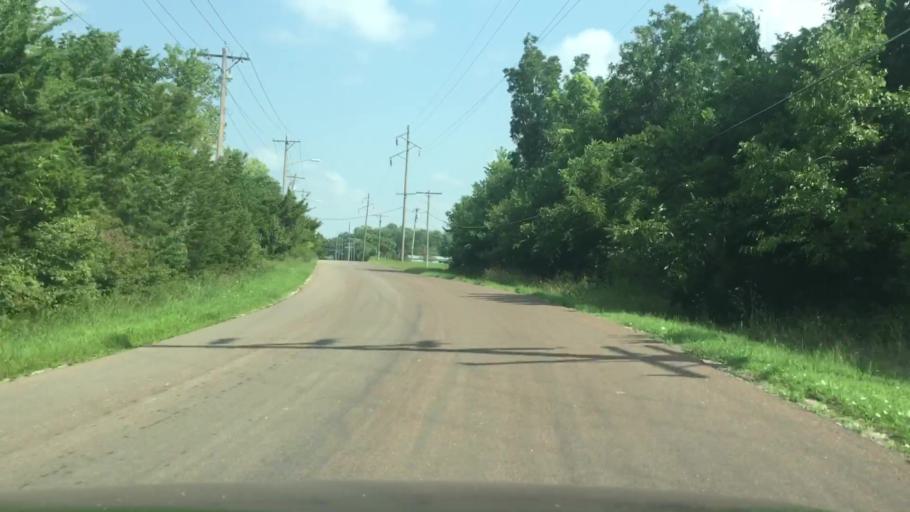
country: US
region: Kansas
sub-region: Allen County
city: Iola
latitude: 37.9062
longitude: -95.4056
